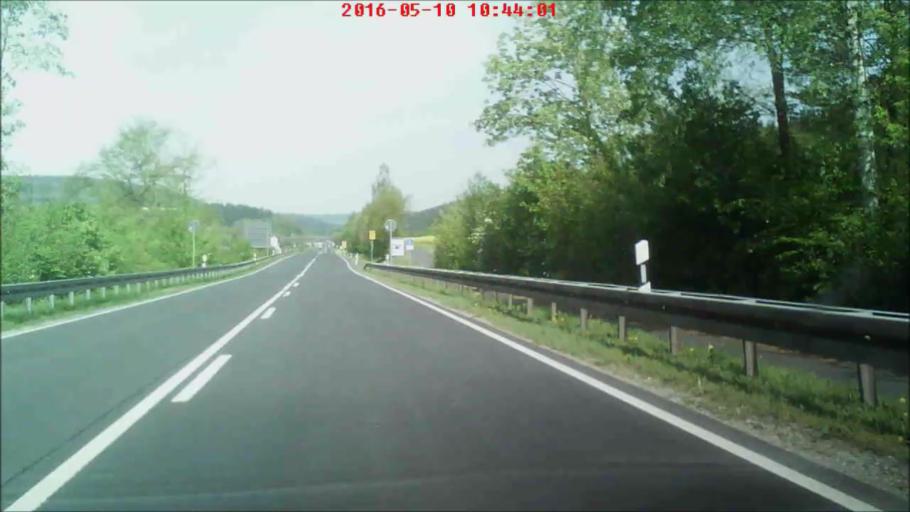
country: DE
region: Hesse
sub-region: Regierungsbezirk Kassel
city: Burghaun
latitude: 50.7144
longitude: 9.7176
